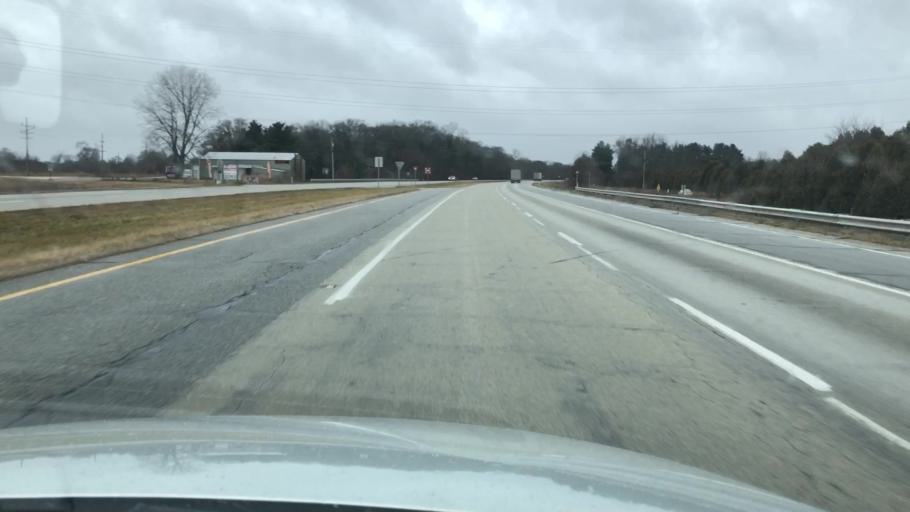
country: US
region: Indiana
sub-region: Starke County
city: Koontz Lake
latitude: 41.3800
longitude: -86.5622
